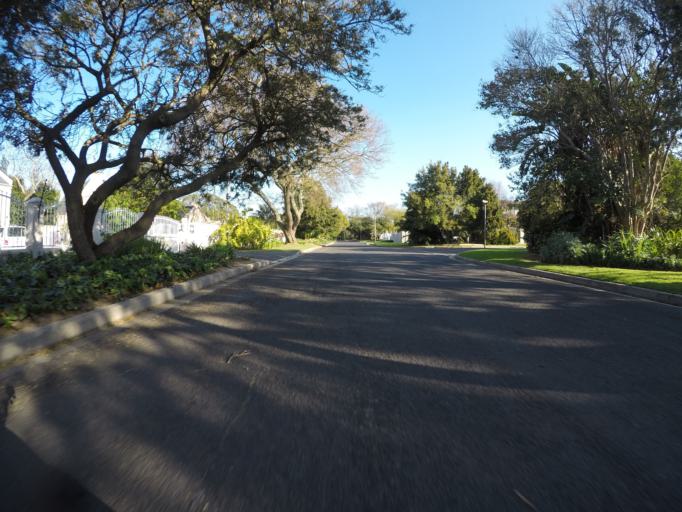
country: ZA
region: Western Cape
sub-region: City of Cape Town
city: Kraaifontein
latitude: -33.8619
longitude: 18.6494
